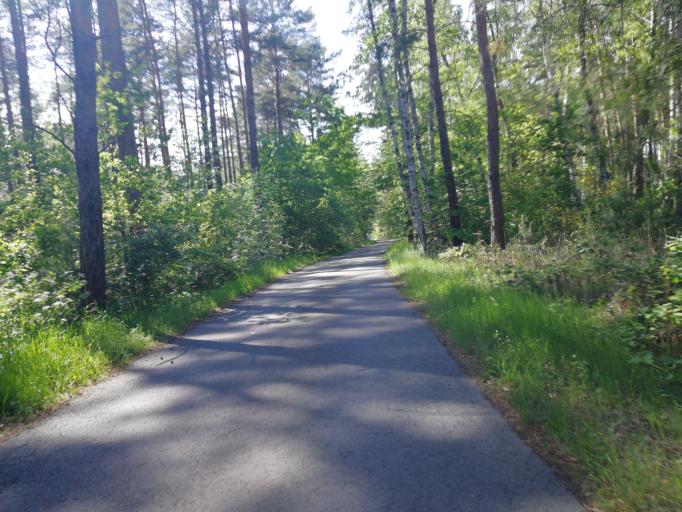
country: DE
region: Brandenburg
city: Calau
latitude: 51.7227
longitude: 13.9260
